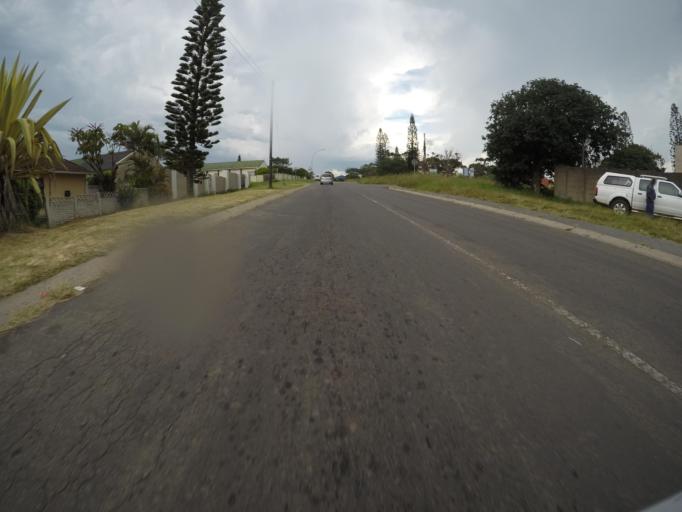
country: ZA
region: Eastern Cape
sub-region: Buffalo City Metropolitan Municipality
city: East London
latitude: -33.0240
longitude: 27.8596
